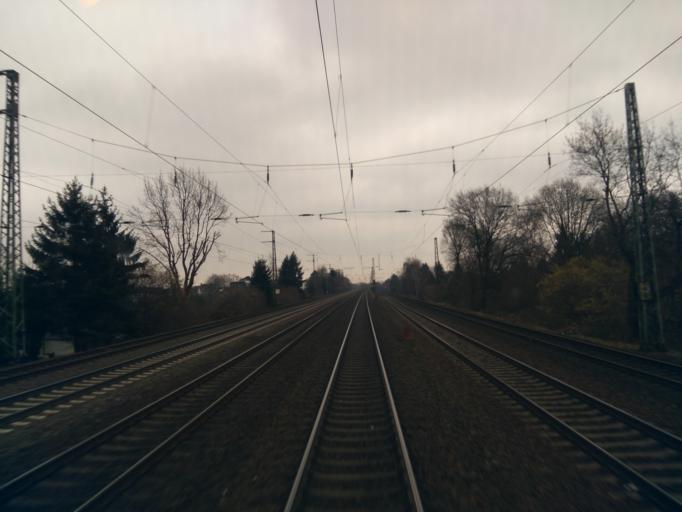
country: DE
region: Bremen
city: Bremen
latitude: 53.0766
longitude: 8.8484
